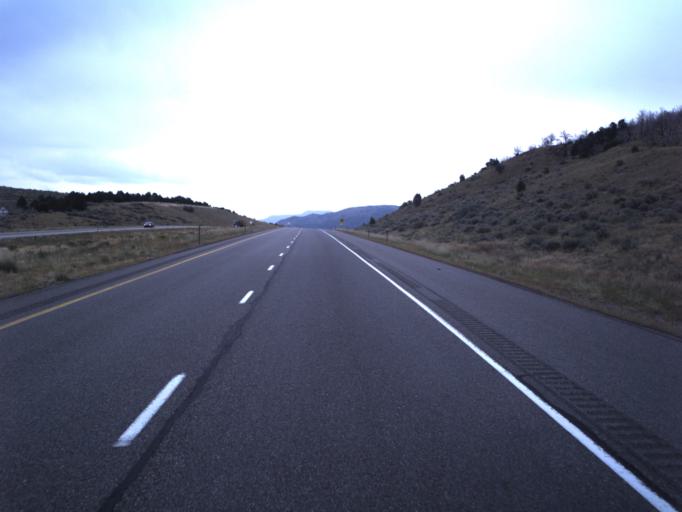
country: US
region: Utah
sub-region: Sevier County
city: Monroe
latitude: 38.5539
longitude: -112.4196
